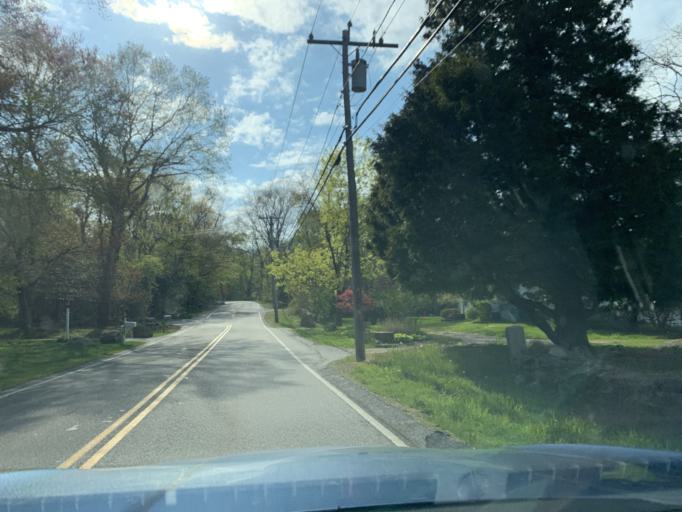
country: US
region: Rhode Island
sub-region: Washington County
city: Exeter
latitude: 41.5949
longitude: -71.5070
